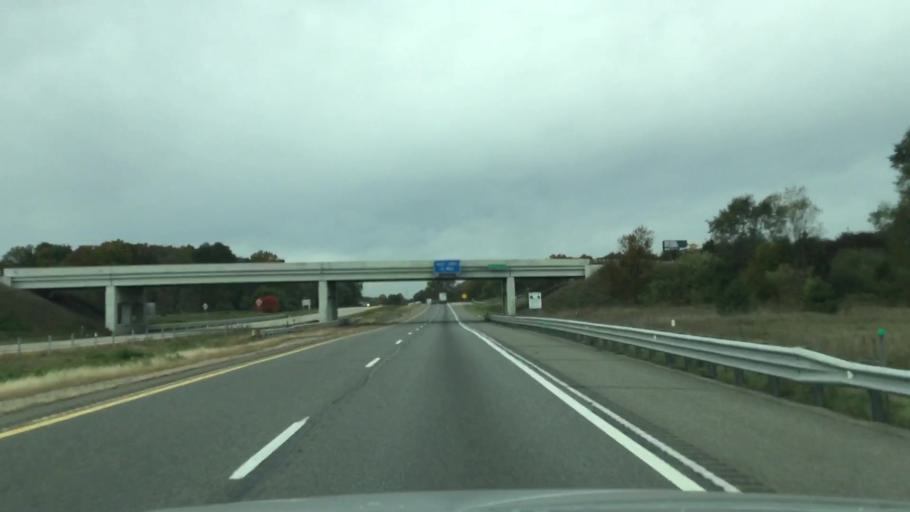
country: US
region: Michigan
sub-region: Jackson County
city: Grass Lake
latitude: 42.2911
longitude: -84.2032
